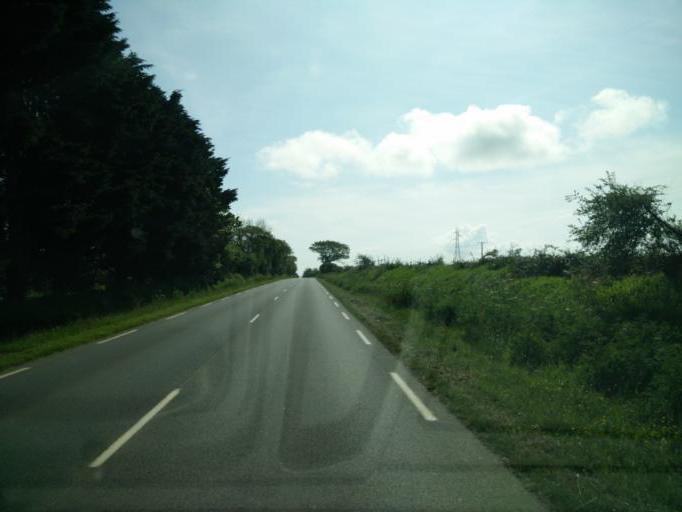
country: FR
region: Brittany
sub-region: Departement du Finistere
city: Lanveoc
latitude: 48.2477
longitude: -4.4300
